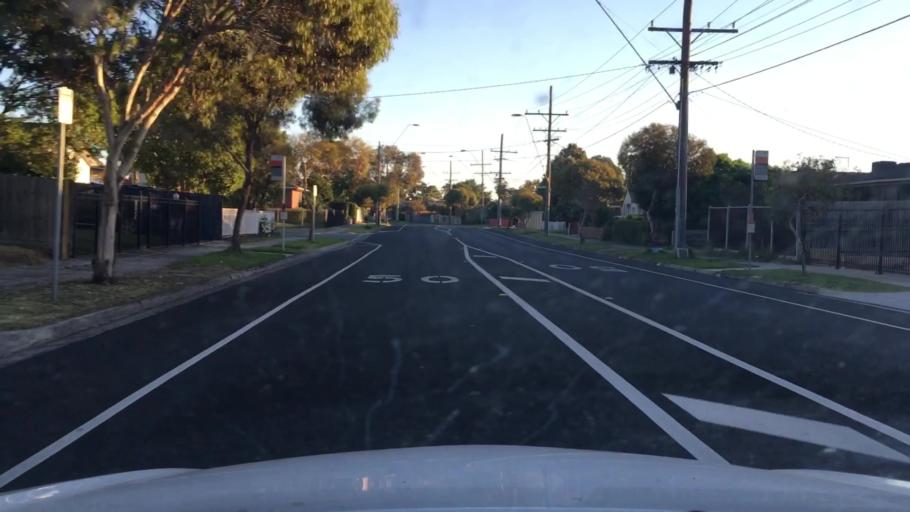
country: AU
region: Victoria
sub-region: Greater Dandenong
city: Keysborough
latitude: -37.9888
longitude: 145.1702
